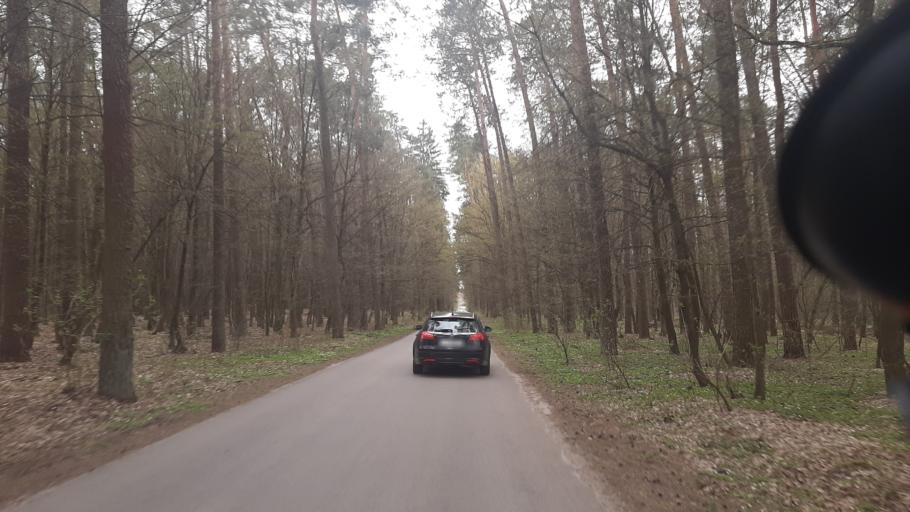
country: PL
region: Lublin Voivodeship
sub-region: Powiat lubelski
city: Niemce
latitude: 51.3733
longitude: 22.5526
